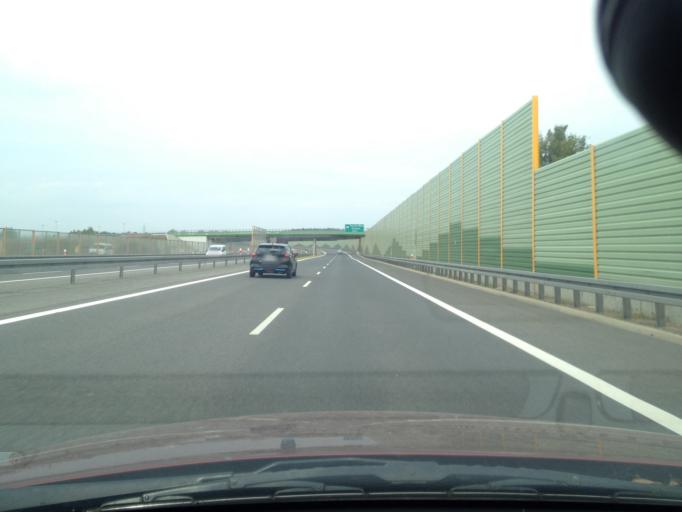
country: PL
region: Lubusz
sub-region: Powiat gorzowski
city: Deszczno
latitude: 52.6892
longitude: 15.2799
